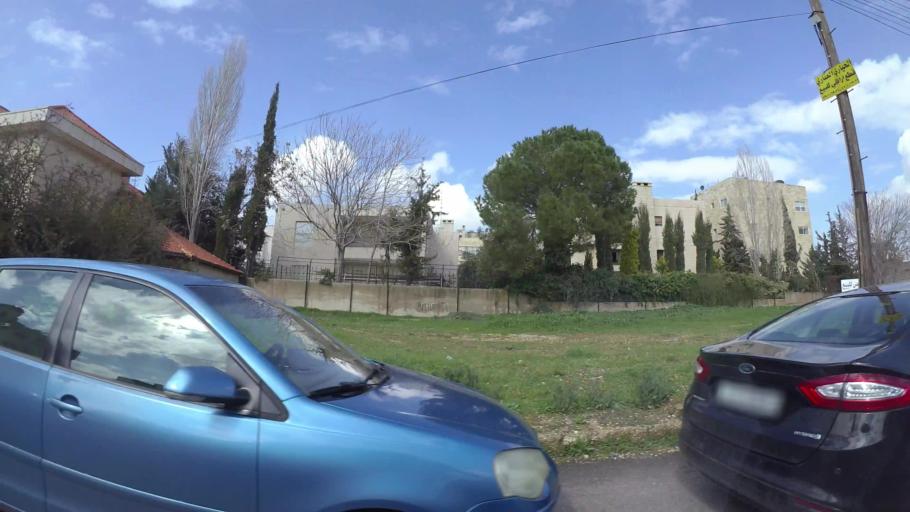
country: JO
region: Amman
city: Amman
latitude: 31.9681
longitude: 35.8927
